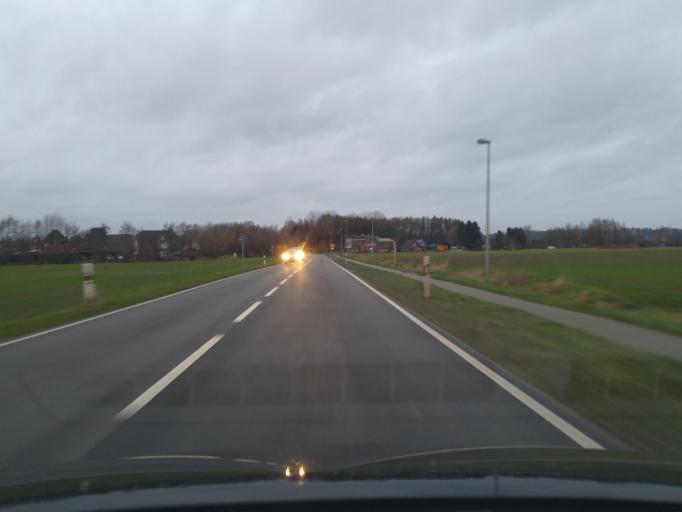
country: DE
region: Schleswig-Holstein
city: Lauenburg
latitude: 53.3508
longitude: 10.5664
